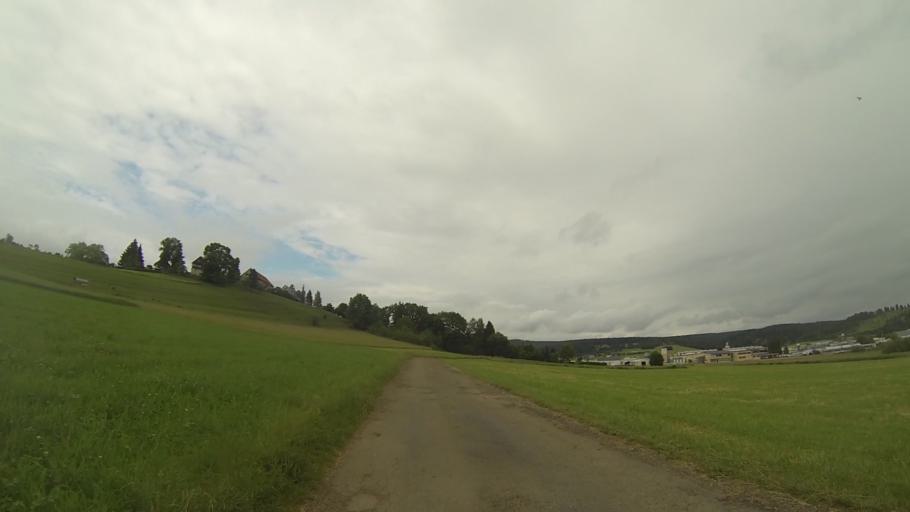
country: DE
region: Baden-Wuerttemberg
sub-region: Regierungsbezirk Stuttgart
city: Steinheim am Albuch
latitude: 48.6850
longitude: 10.0731
